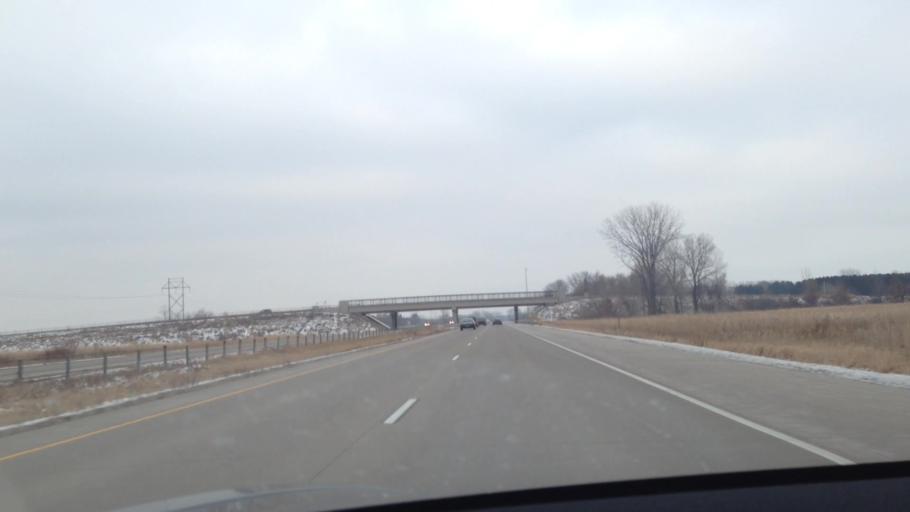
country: US
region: Minnesota
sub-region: Anoka County
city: Lino Lakes
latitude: 45.1917
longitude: -93.0762
